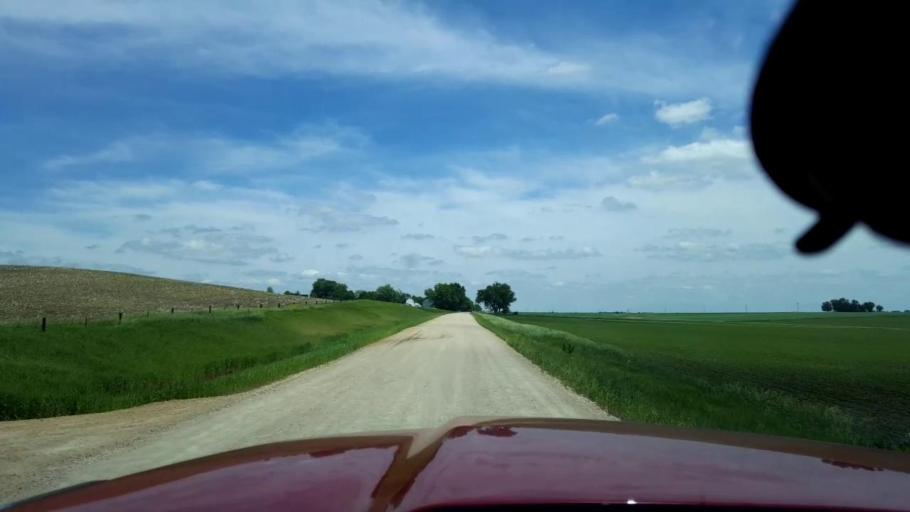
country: US
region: Iowa
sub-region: Linn County
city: Lisbon
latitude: 41.9563
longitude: -91.3657
